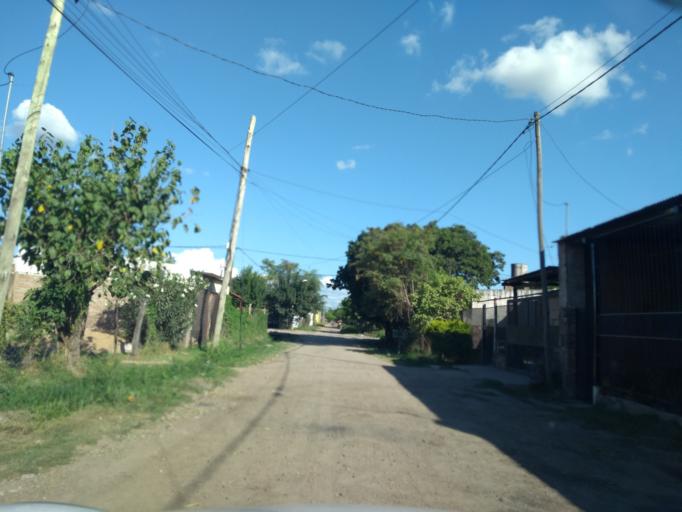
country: AR
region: Chaco
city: Resistencia
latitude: -27.4771
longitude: -58.9768
